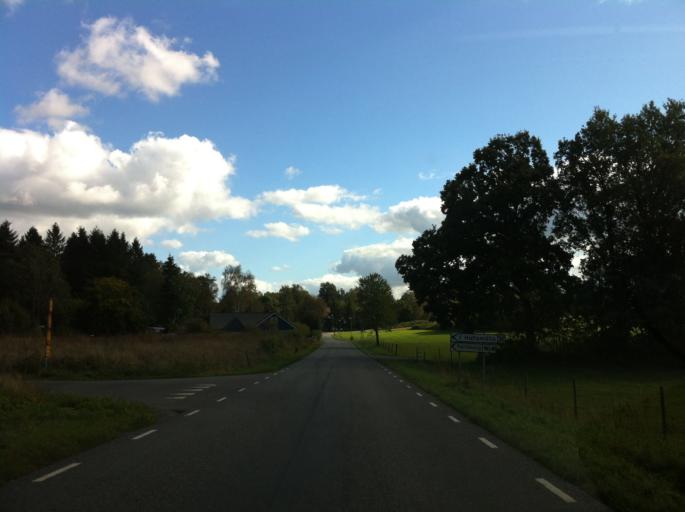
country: SE
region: Skane
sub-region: Kristianstads Kommun
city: Degeberga
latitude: 55.7062
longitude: 13.9973
